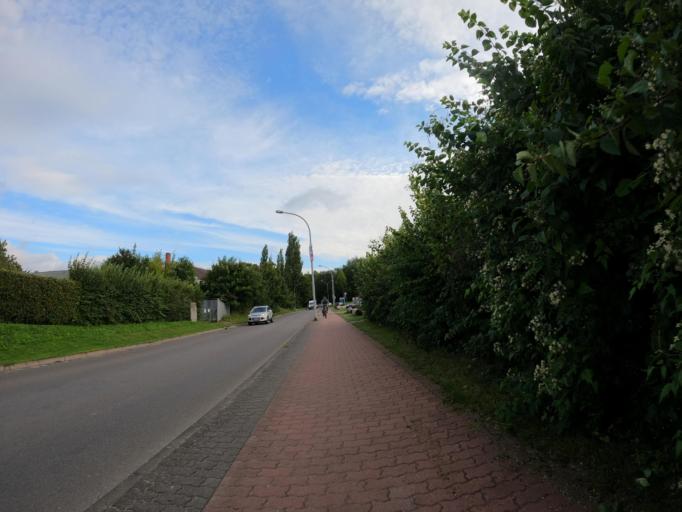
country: DE
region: Mecklenburg-Vorpommern
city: Kramerhof
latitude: 54.3349
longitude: 13.0646
